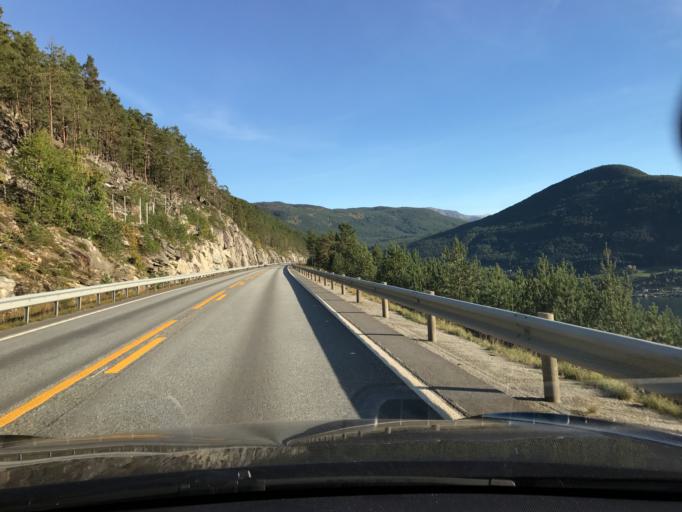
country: NO
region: Sogn og Fjordane
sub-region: Sogndal
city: Sogndalsfjora
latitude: 61.1879
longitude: 7.2397
